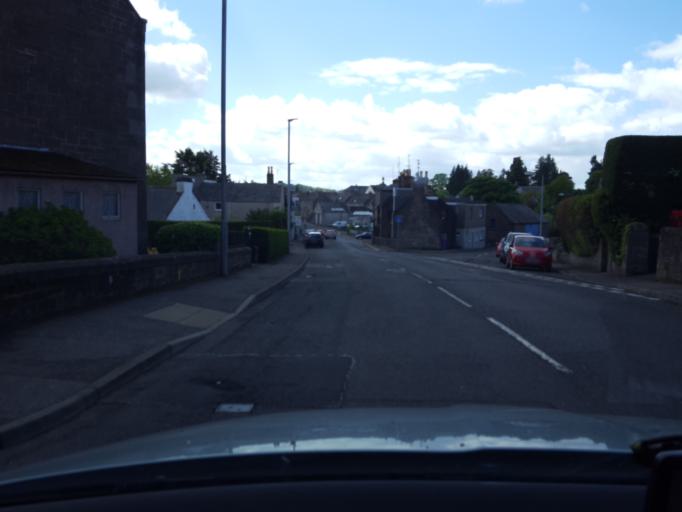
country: GB
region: Scotland
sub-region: Angus
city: Brechin
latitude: 56.7366
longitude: -2.6584
